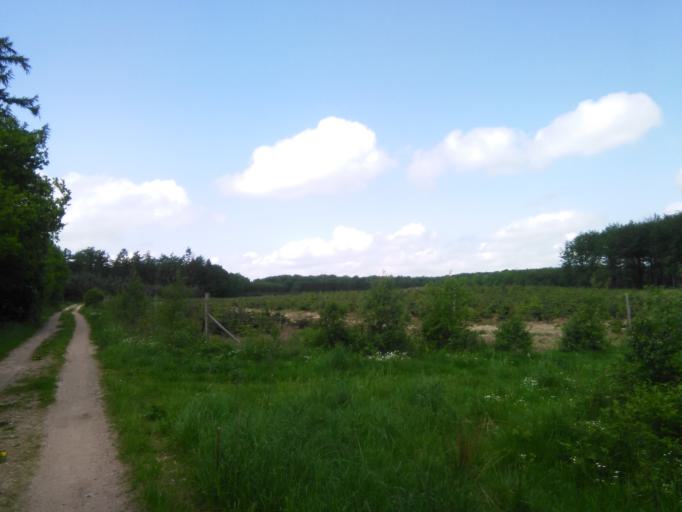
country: DK
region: Central Jutland
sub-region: Favrskov Kommune
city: Hinnerup
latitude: 56.2575
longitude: 10.0405
